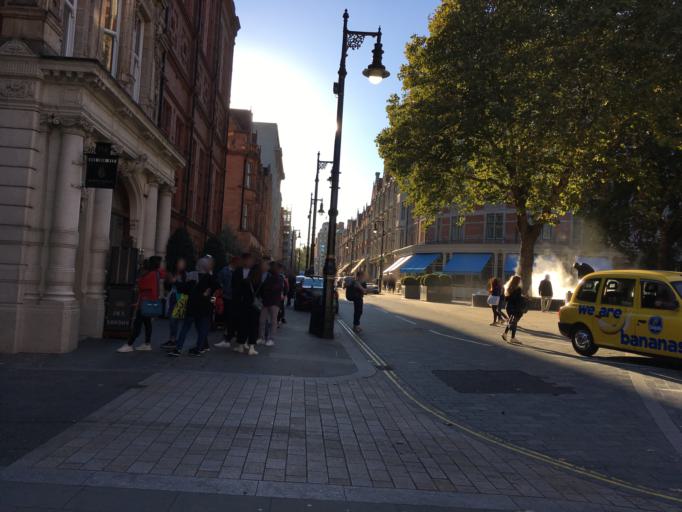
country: GB
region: England
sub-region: Greater London
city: London
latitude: 51.5101
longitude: -0.1487
